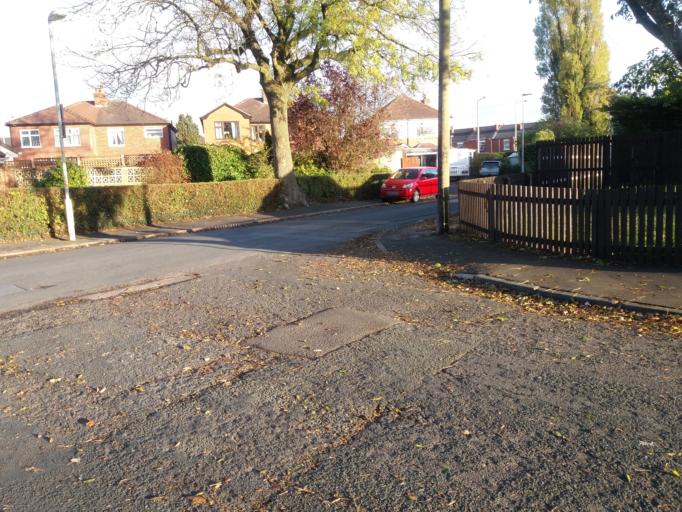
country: GB
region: England
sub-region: Lancashire
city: Coppull
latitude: 53.6277
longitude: -2.6573
